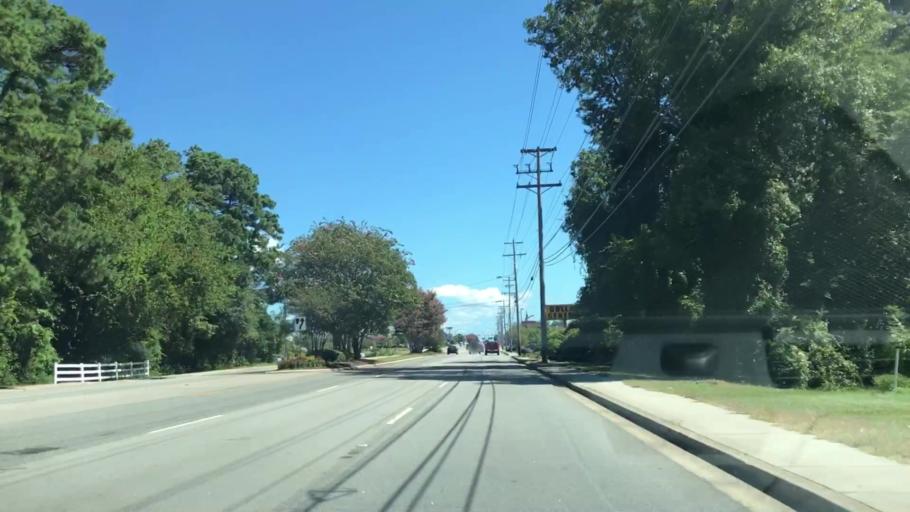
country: US
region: South Carolina
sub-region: Horry County
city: North Myrtle Beach
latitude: 33.8203
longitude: -78.6895
